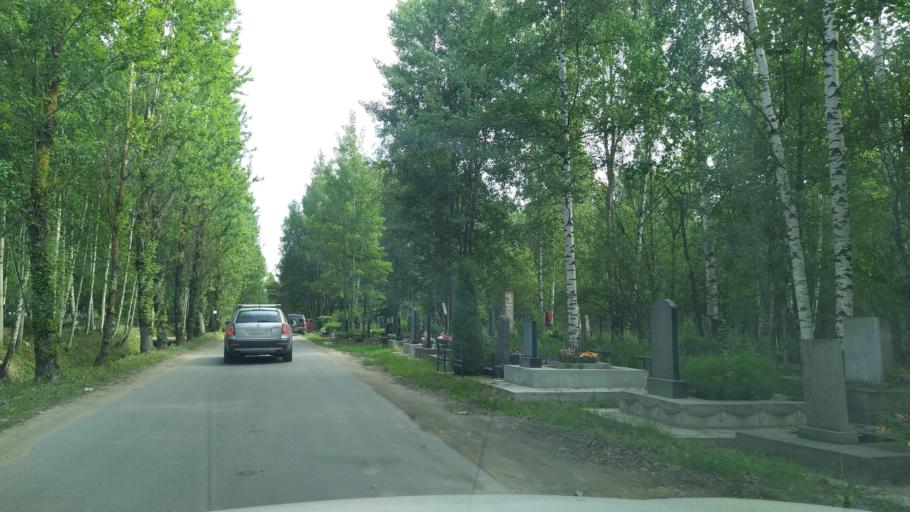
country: RU
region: St.-Petersburg
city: Dachnoye
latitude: 59.7686
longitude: 30.2638
